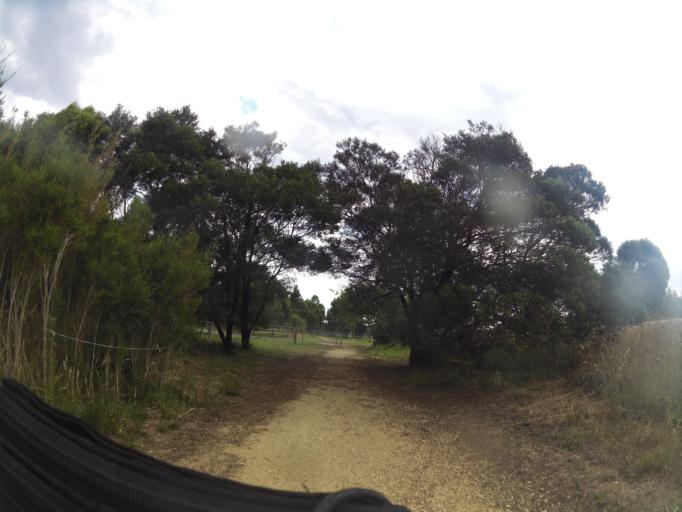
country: AU
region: Victoria
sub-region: Latrobe
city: Traralgon
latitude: -38.0535
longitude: 146.6280
